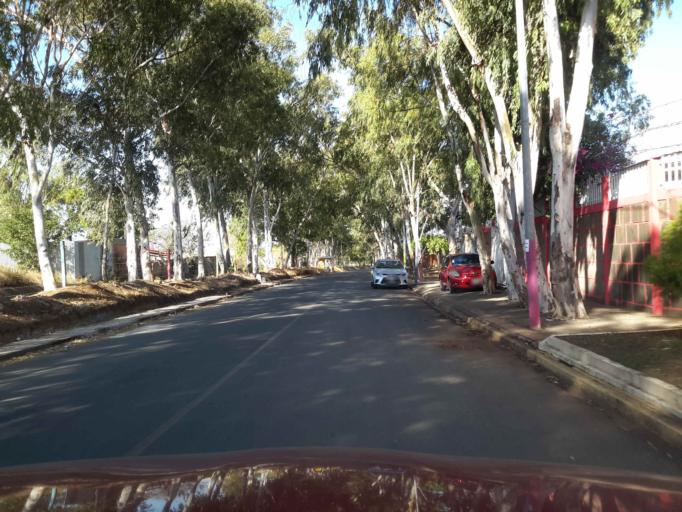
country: NI
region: Managua
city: Managua
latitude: 12.1309
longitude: -86.2735
